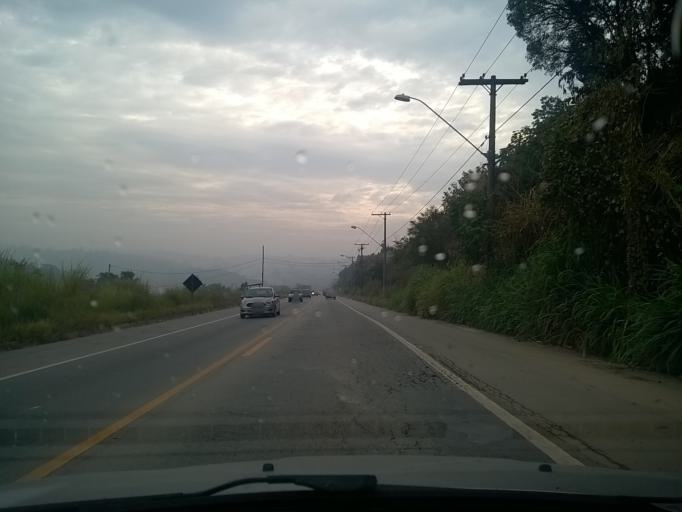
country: BR
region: Sao Paulo
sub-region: Francisco Morato
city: Francisco Morato
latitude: -23.3051
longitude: -46.7571
